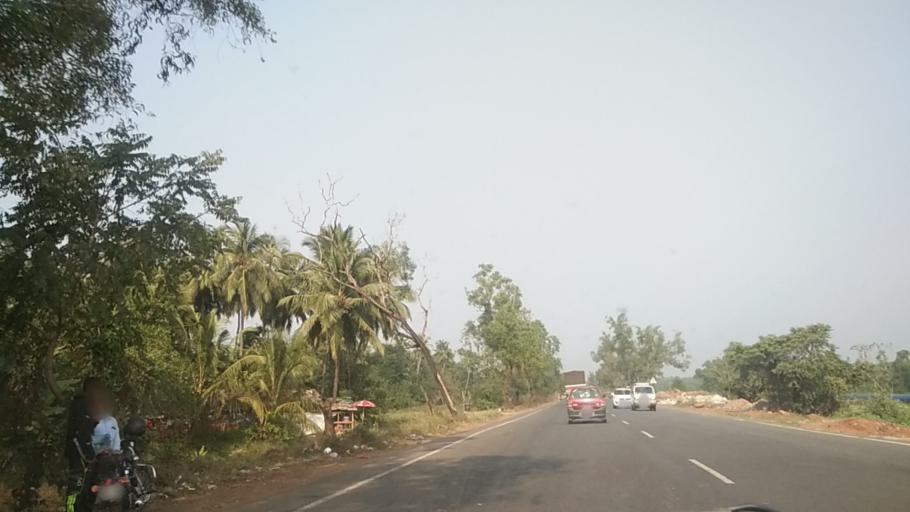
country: IN
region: Goa
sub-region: North Goa
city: Guirim
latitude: 15.5749
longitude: 73.8076
